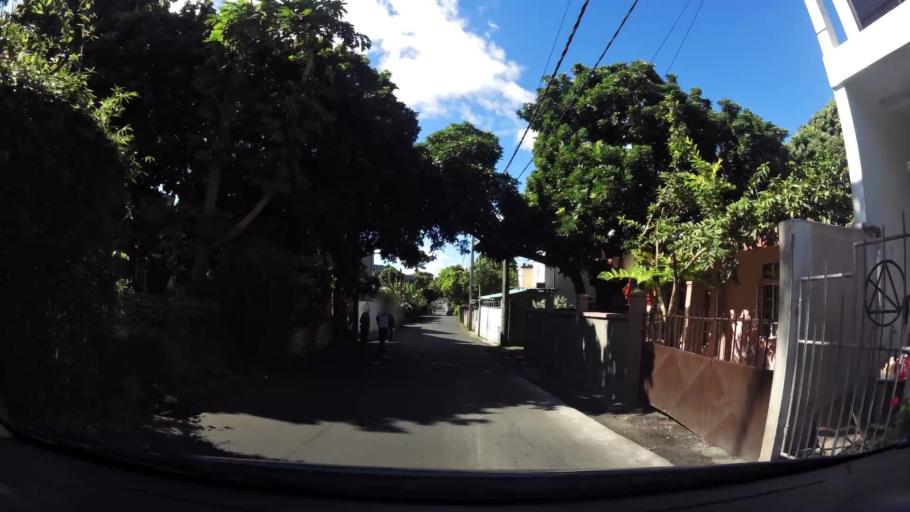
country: MU
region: Plaines Wilhems
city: Vacoas
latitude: -20.3087
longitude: 57.4810
